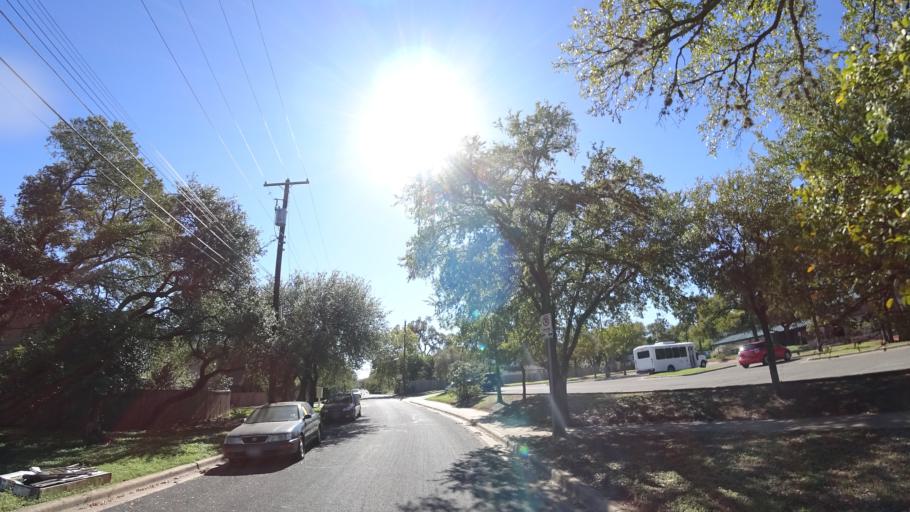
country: US
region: Texas
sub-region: Travis County
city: Rollingwood
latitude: 30.2331
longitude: -97.7837
